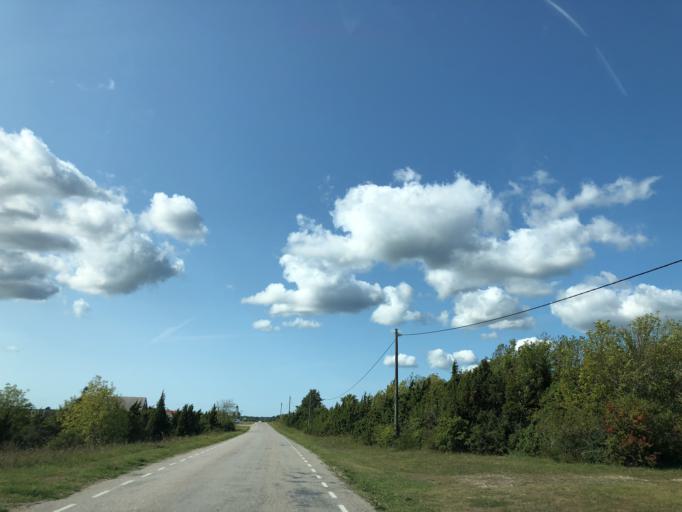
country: EE
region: Hiiumaa
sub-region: Kaerdla linn
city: Kardla
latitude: 58.7878
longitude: 22.7766
